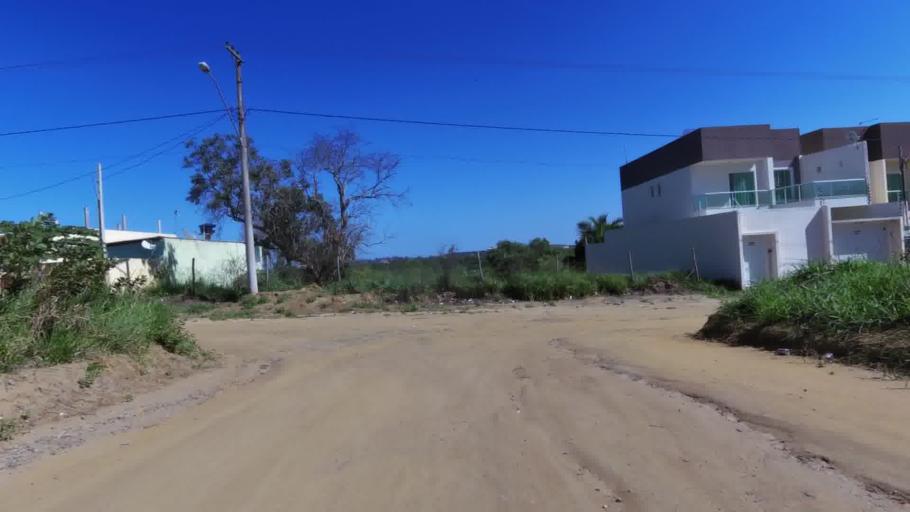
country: BR
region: Espirito Santo
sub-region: Guarapari
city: Guarapari
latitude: -20.7350
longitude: -40.5477
